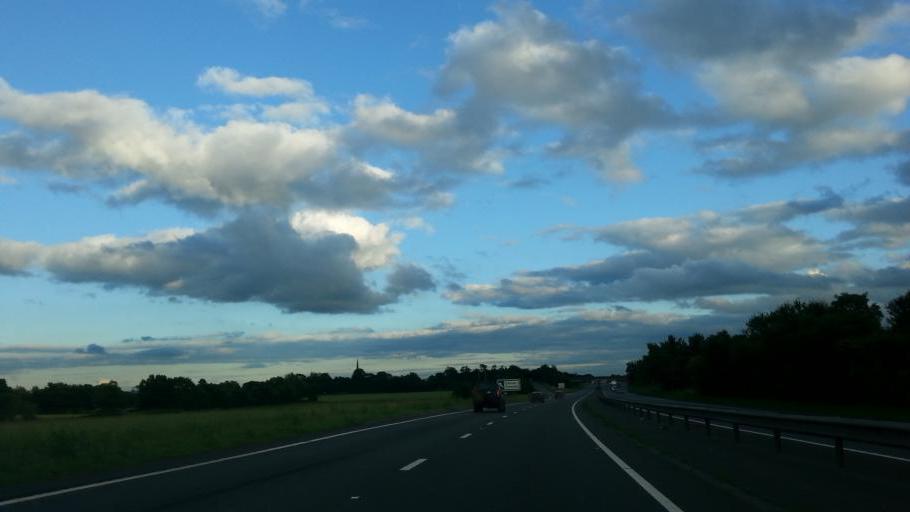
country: GB
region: England
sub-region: Nottinghamshire
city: South Collingham
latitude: 53.1738
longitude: -0.8134
